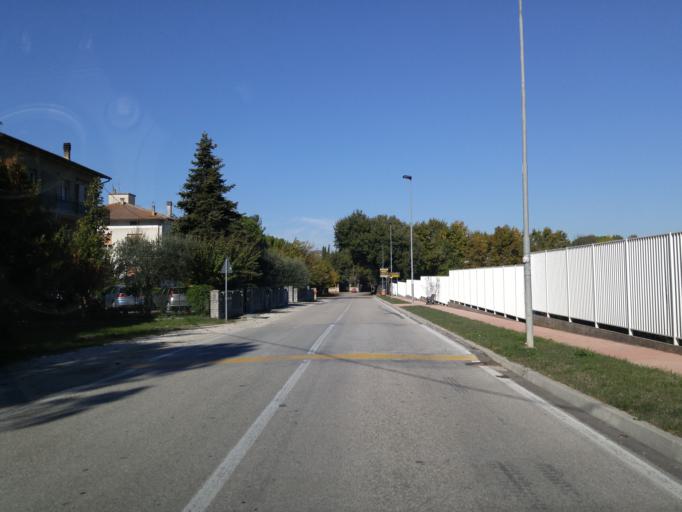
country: IT
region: The Marches
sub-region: Provincia di Pesaro e Urbino
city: Sant'Ippolito
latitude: 43.7019
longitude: 12.8727
